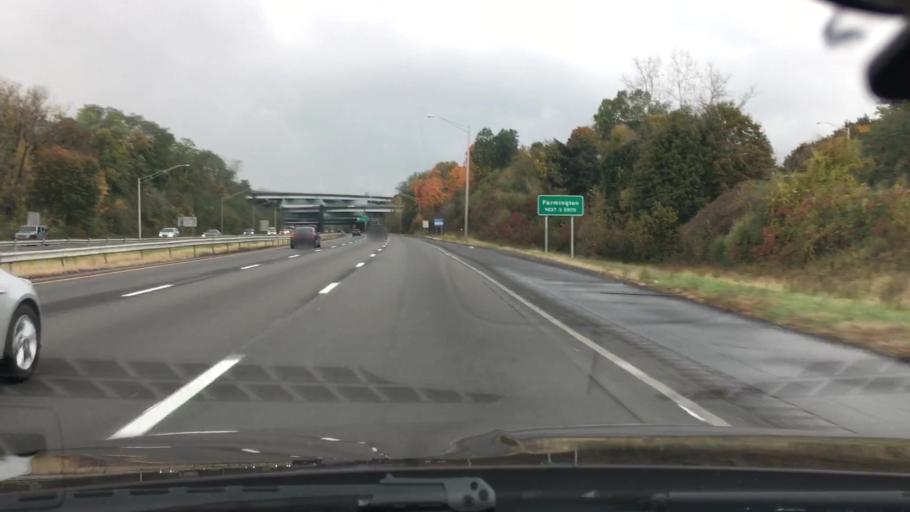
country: US
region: Connecticut
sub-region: Hartford County
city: West Hartford
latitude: 41.7253
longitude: -72.7659
